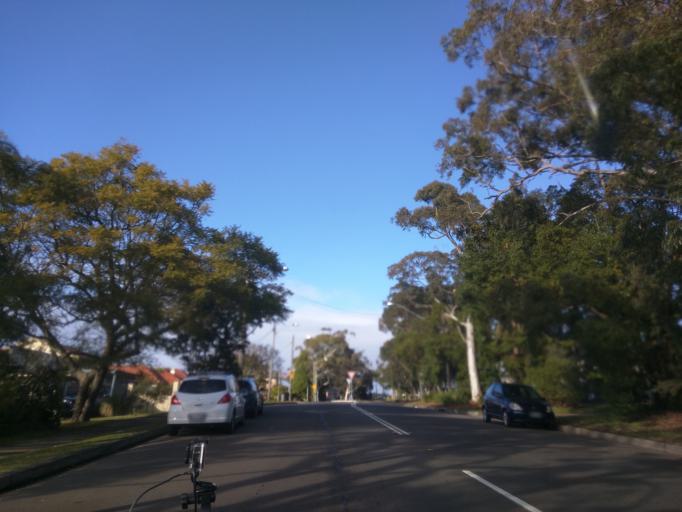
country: AU
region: New South Wales
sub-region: Hurstville
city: Lugarno
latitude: -33.9744
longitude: 151.0481
